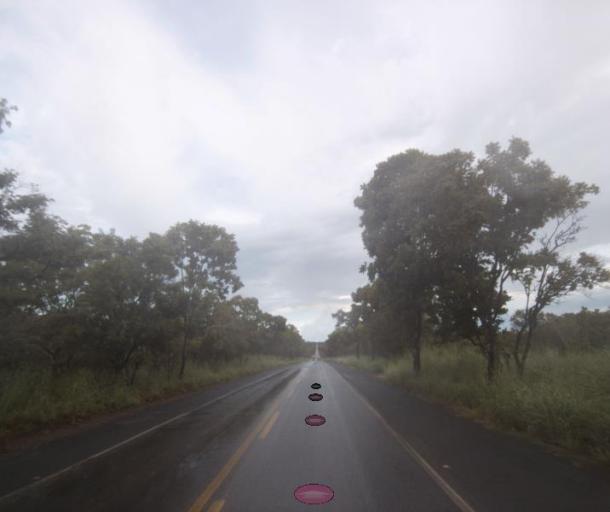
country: BR
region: Goias
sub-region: Porangatu
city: Porangatu
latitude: -13.7960
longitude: -49.0359
